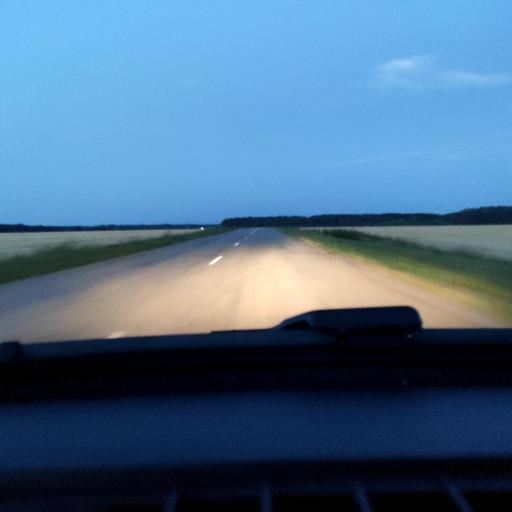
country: RU
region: Lipetsk
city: Zadonsk
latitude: 52.2982
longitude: 38.8108
